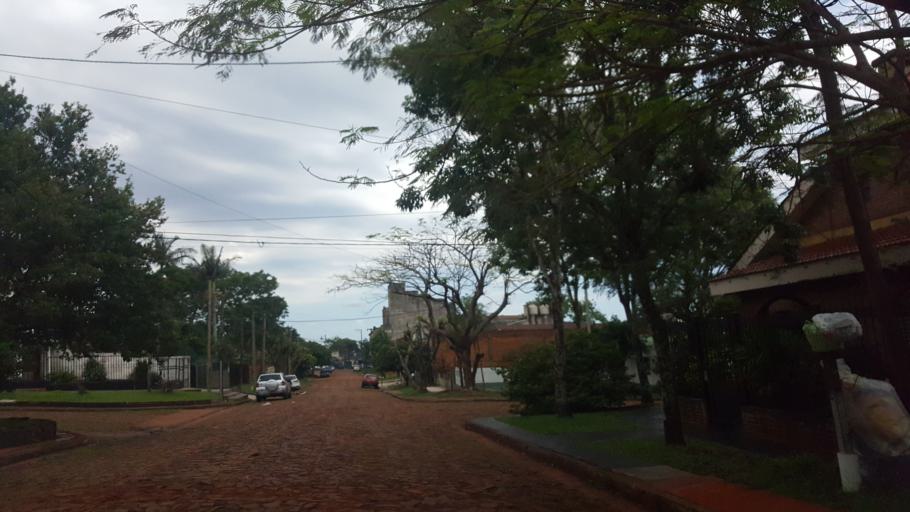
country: AR
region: Misiones
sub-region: Departamento de Capital
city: Posadas
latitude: -27.3982
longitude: -55.9117
